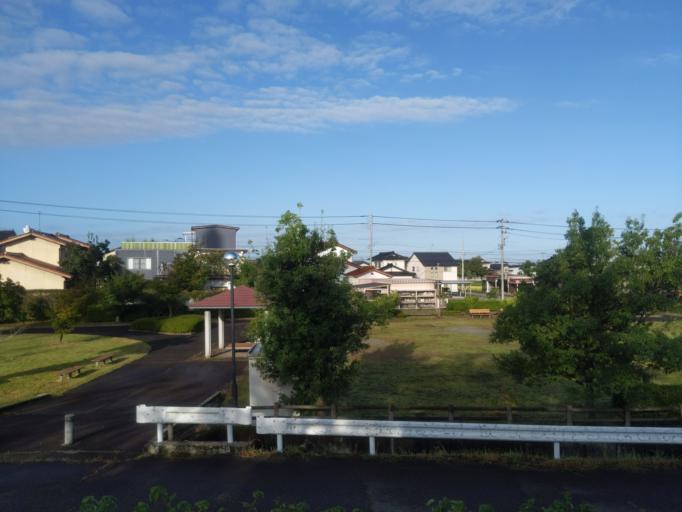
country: JP
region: Toyama
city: Kamiichi
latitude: 36.6672
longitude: 137.3142
